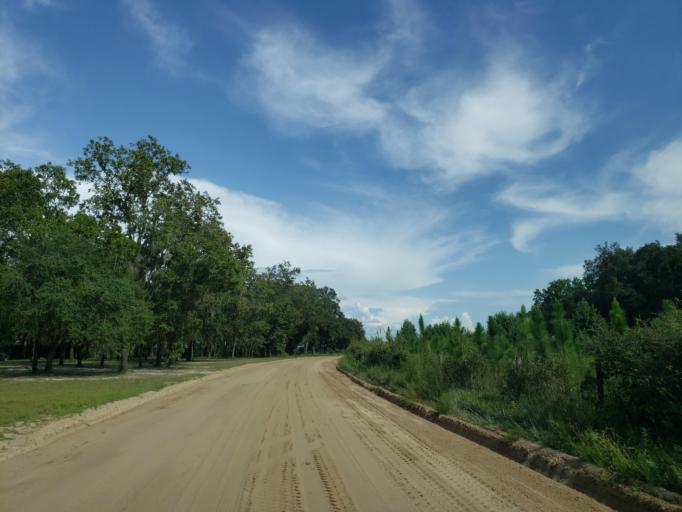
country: US
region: Georgia
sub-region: Echols County
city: Statenville
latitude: 30.6234
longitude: -83.1880
